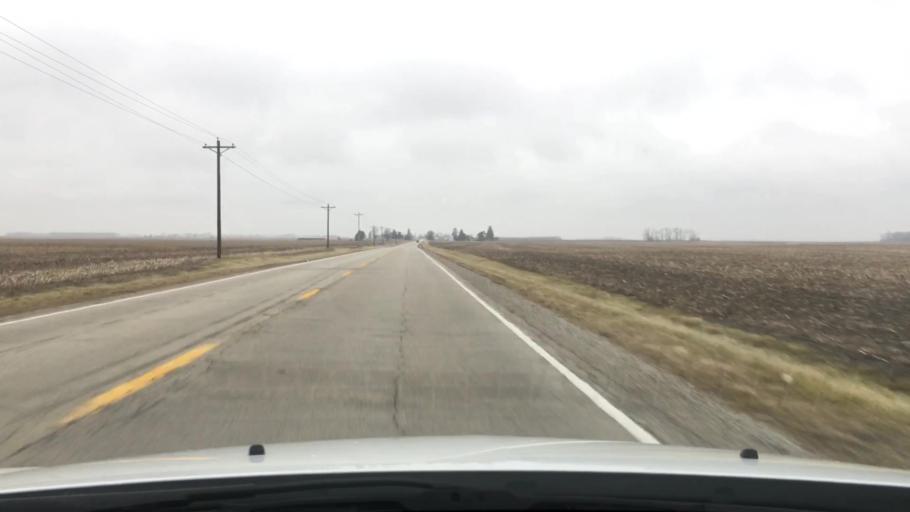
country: US
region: Illinois
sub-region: Iroquois County
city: Watseka
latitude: 40.8906
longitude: -87.6925
